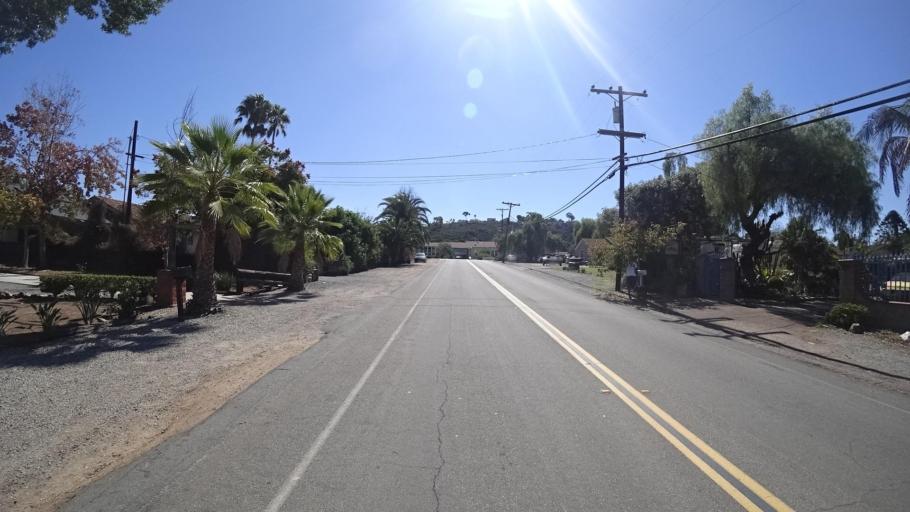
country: US
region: California
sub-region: San Diego County
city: Bonita
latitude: 32.6575
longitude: -117.0339
